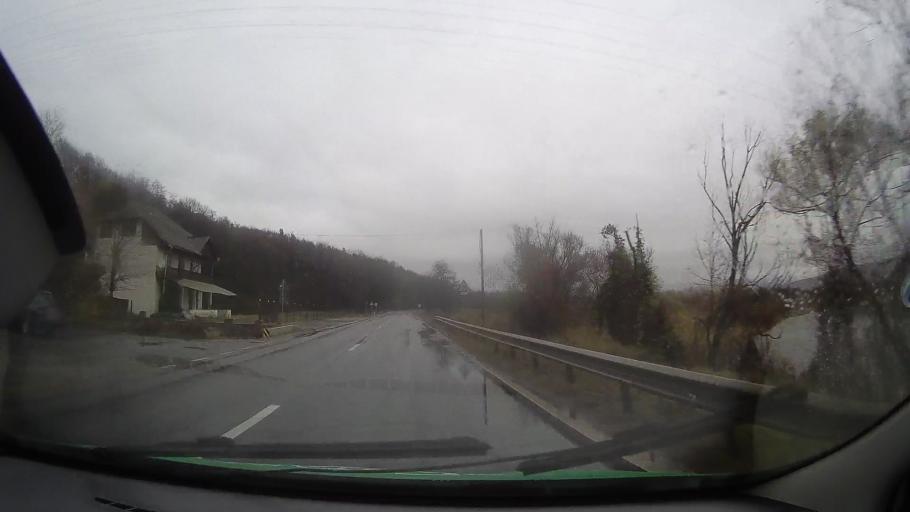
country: RO
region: Mures
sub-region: Comuna Brancovenesti
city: Valenii de Mures
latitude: 46.8777
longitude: 24.7771
